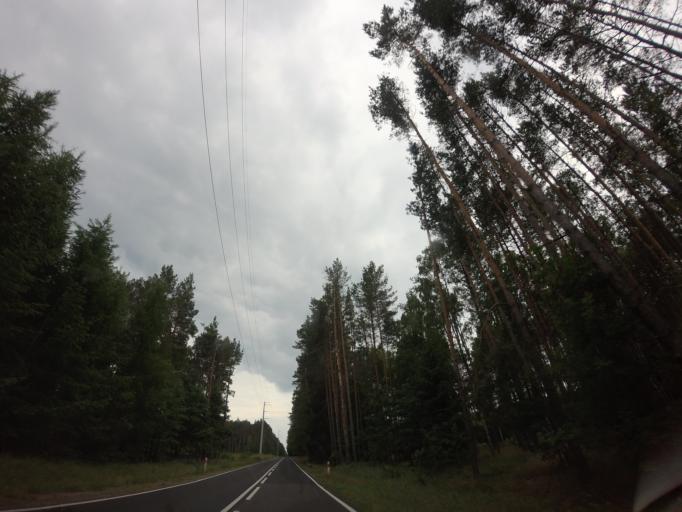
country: PL
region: West Pomeranian Voivodeship
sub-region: Powiat drawski
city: Czaplinek
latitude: 53.4842
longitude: 16.2288
